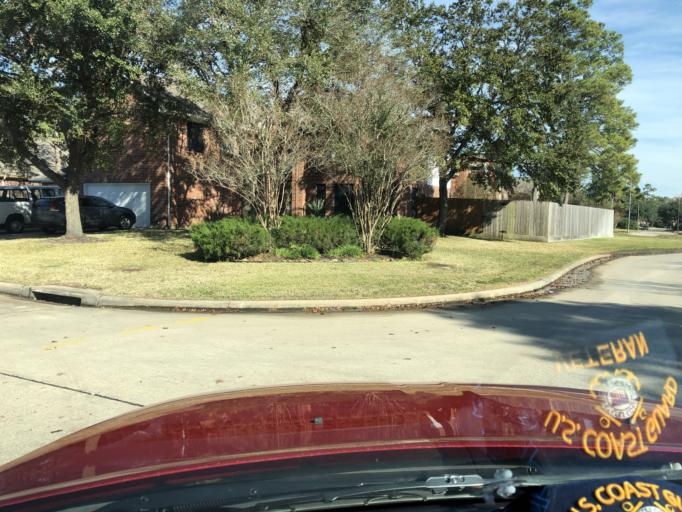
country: US
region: Texas
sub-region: Harris County
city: Tomball
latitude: 30.0216
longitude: -95.5568
